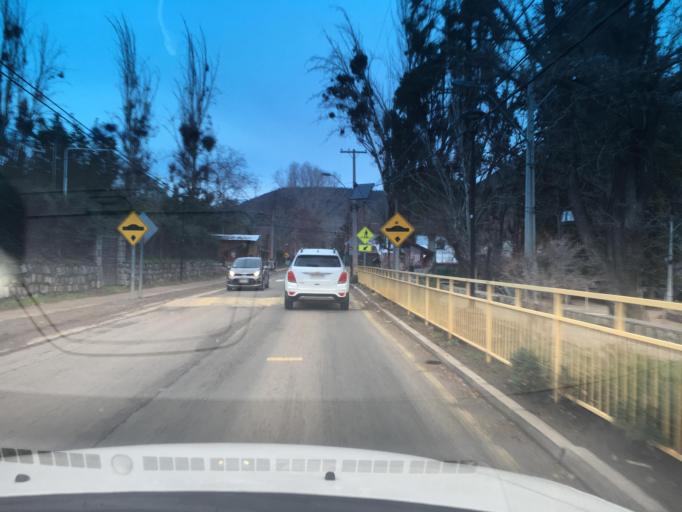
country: CL
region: Santiago Metropolitan
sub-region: Provincia de Cordillera
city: Puente Alto
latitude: -33.7282
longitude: -70.3179
